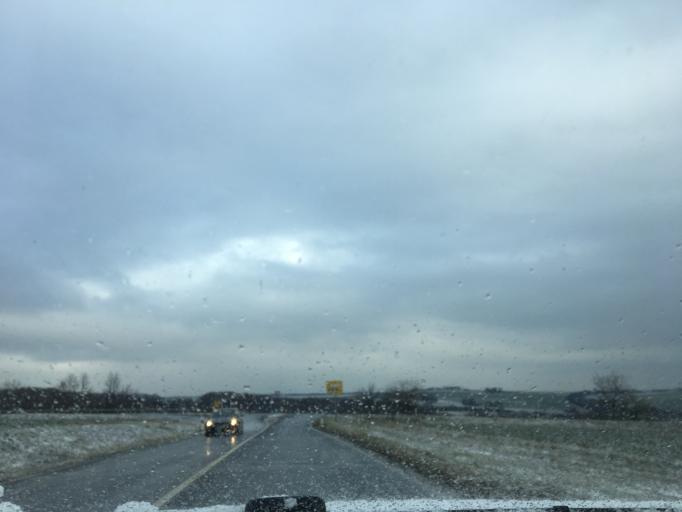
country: DE
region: Rheinland-Pfalz
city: Kirchheimbolanden
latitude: 49.6734
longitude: 7.9947
